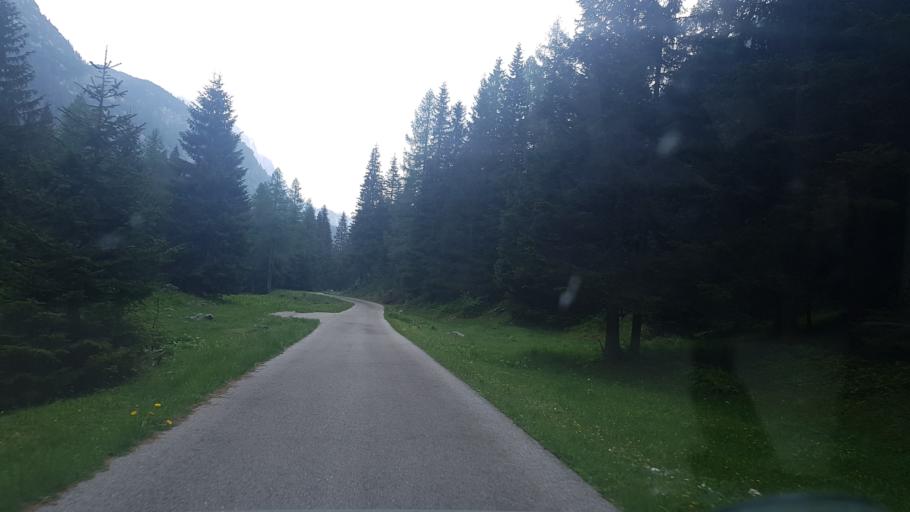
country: IT
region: Friuli Venezia Giulia
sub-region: Provincia di Udine
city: Paularo
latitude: 46.5627
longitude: 13.1758
